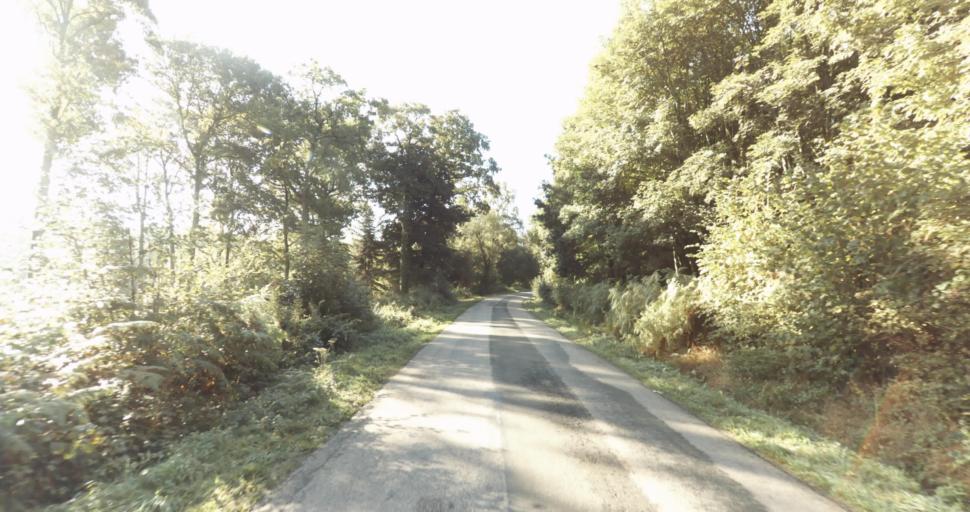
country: FR
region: Lower Normandy
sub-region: Departement de l'Orne
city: Vimoutiers
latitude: 48.9201
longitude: 0.2488
